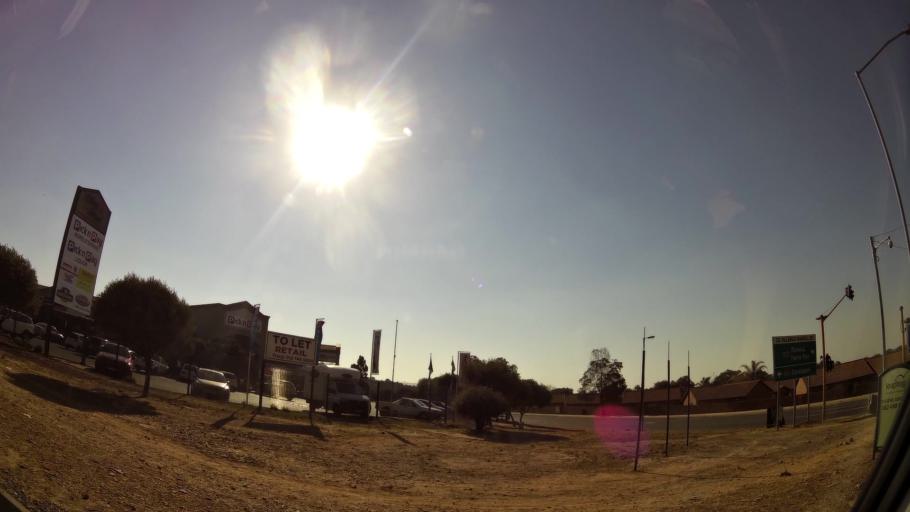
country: ZA
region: Gauteng
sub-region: City of Tshwane Metropolitan Municipality
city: Centurion
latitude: -25.8298
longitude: 28.2963
